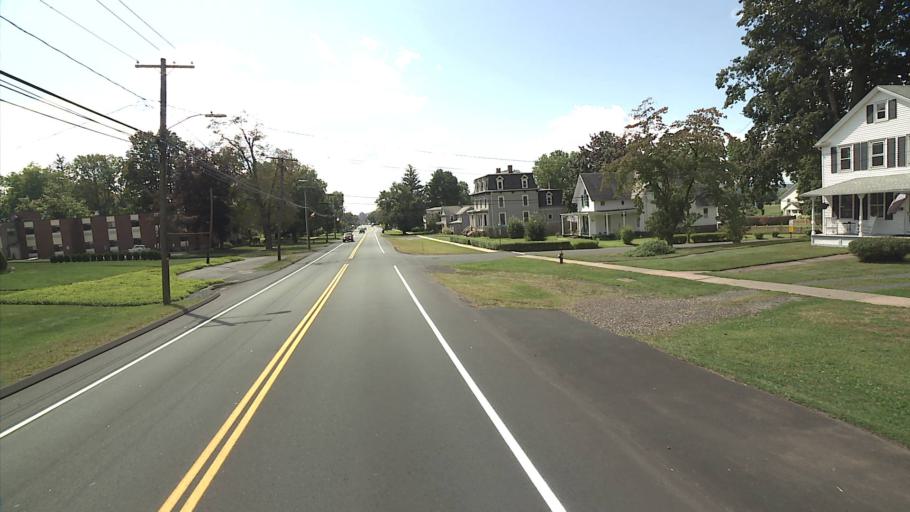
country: US
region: Connecticut
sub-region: Middlesex County
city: Portland
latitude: 41.5793
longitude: -72.6358
